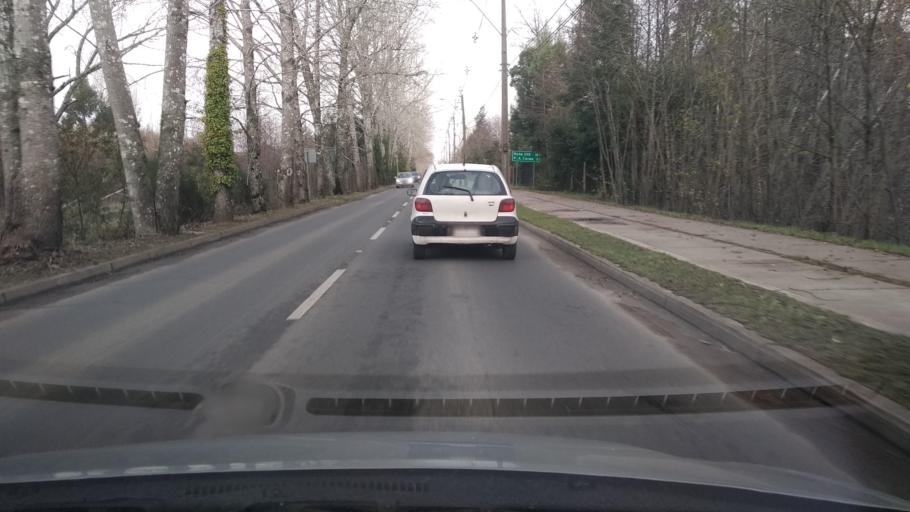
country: CL
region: Los Rios
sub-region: Provincia de Valdivia
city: Valdivia
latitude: -39.7998
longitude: -73.2480
